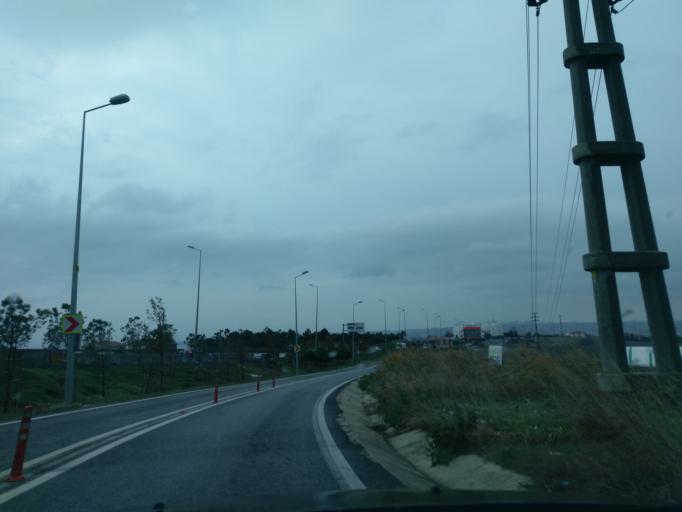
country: TR
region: Istanbul
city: Bueyuekcekmece
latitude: 41.0262
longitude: 28.6078
